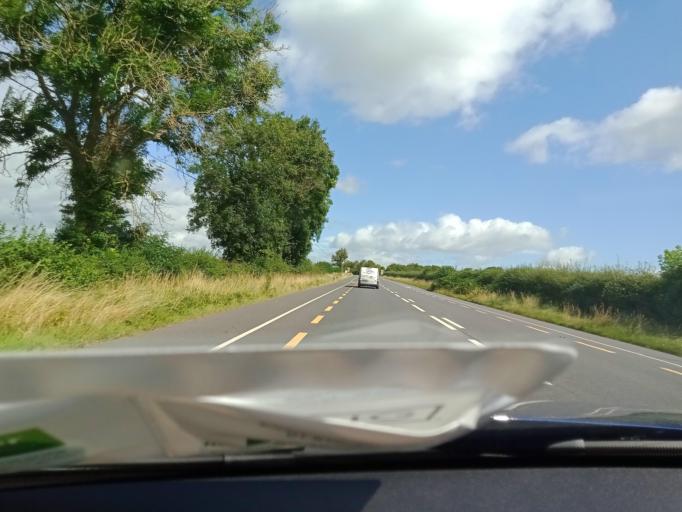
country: IE
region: Leinster
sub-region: Laois
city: Abbeyleix
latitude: 52.8681
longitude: -7.3659
